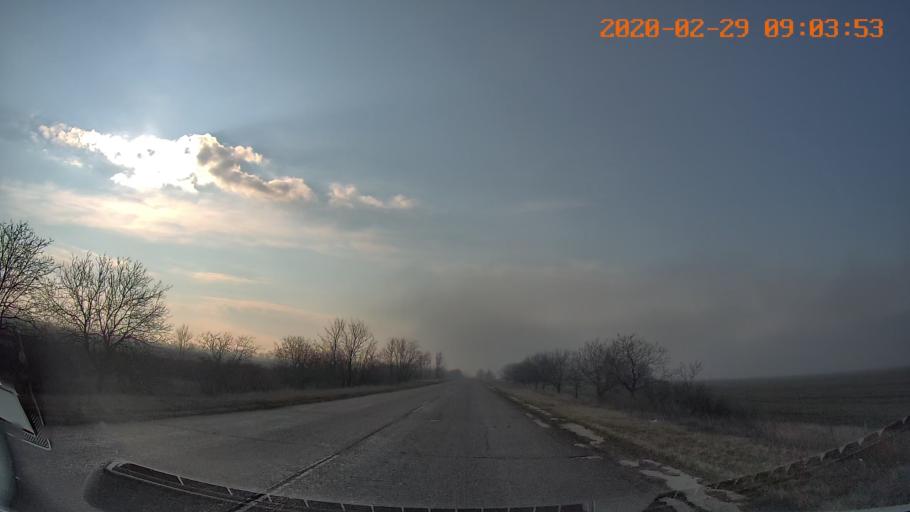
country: UA
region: Odessa
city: Velykoploske
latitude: 46.9103
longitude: 29.7336
